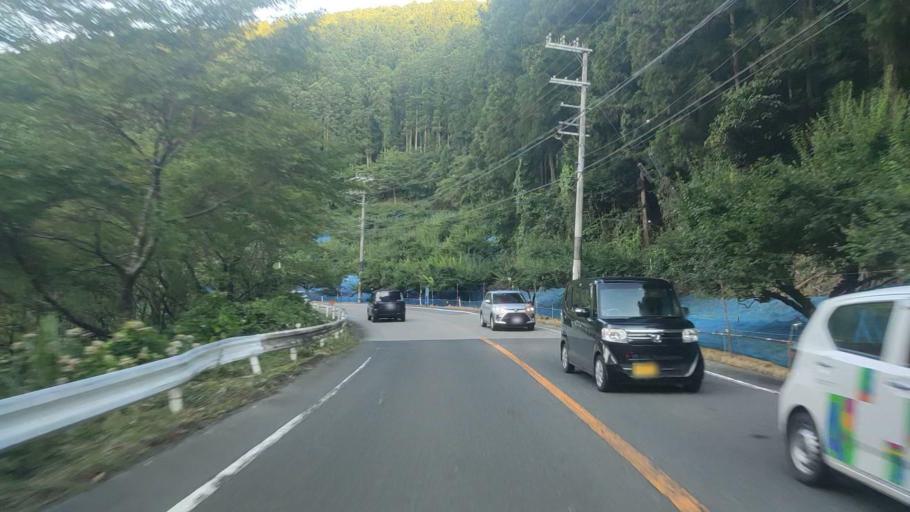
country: JP
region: Wakayama
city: Tanabe
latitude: 33.8170
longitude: 135.5569
